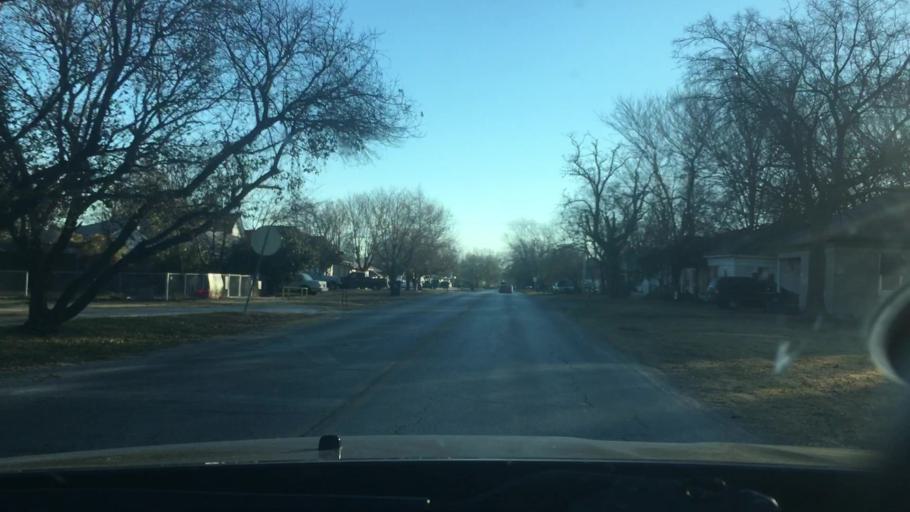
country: US
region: Oklahoma
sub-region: Pontotoc County
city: Ada
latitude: 34.7713
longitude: -96.6881
